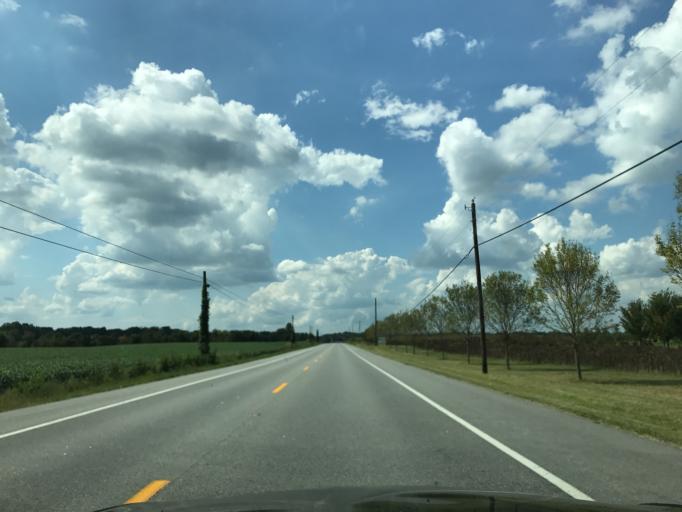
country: US
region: Maryland
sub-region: Queen Anne's County
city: Kingstown
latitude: 39.1855
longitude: -75.8769
